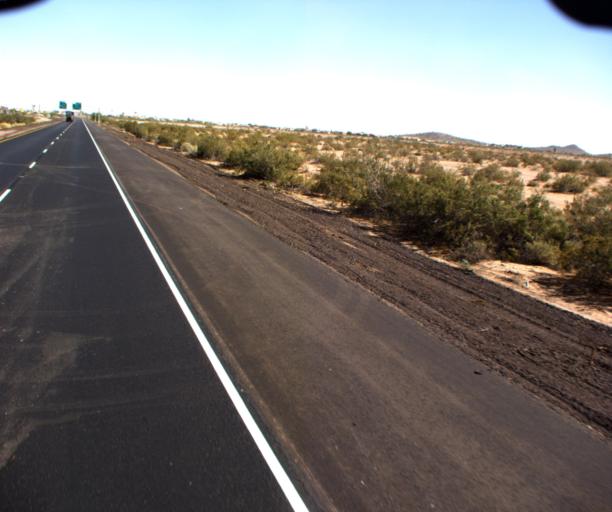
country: US
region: Arizona
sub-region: Pinal County
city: Arizona City
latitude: 32.8224
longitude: -111.6927
